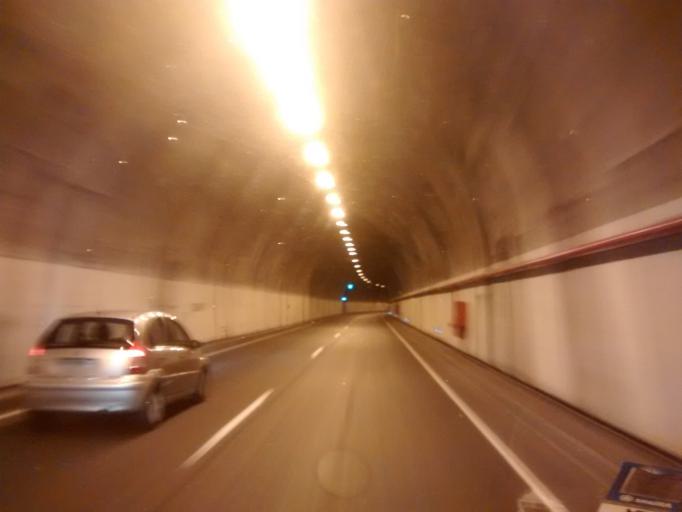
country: PT
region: Madeira
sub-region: Ribeira Brava
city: Campanario
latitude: 32.6584
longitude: -17.0170
